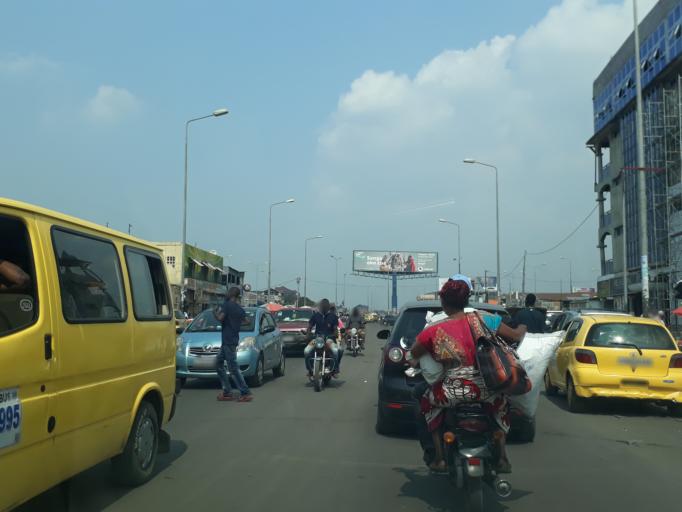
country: CD
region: Kinshasa
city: Kinshasa
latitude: -4.3391
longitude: 15.3080
